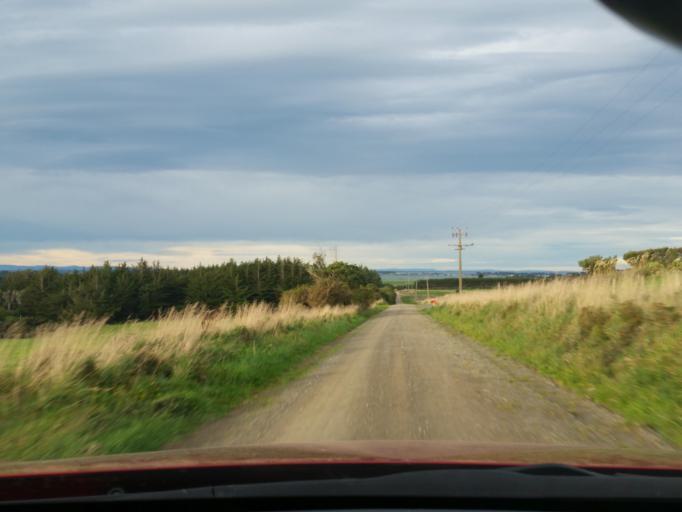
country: NZ
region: Southland
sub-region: Southland District
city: Riverton
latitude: -46.3418
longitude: 167.9381
